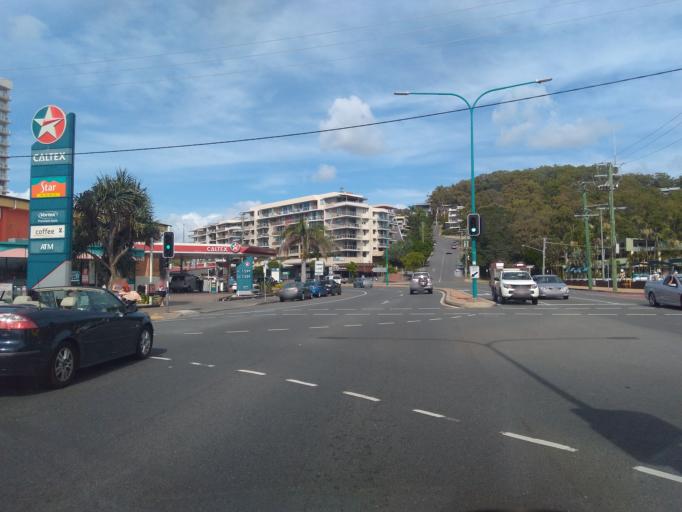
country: AU
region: Queensland
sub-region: Gold Coast
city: Burleigh Waters
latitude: -28.0895
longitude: 153.4530
